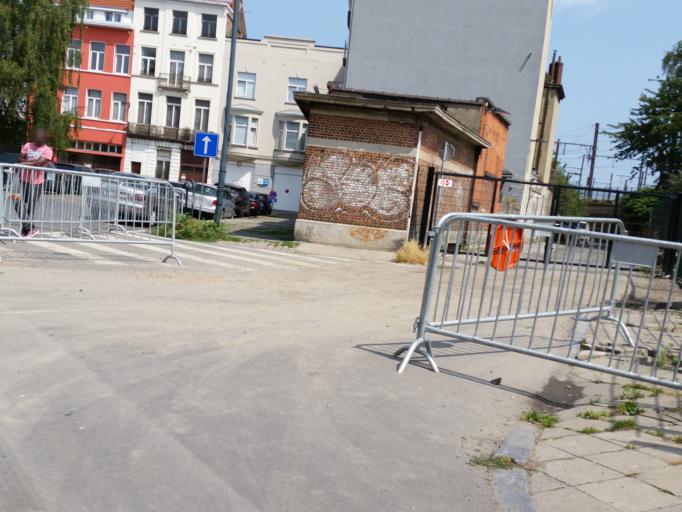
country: BE
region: Brussels Capital
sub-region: Bruxelles-Capitale
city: Brussels
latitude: 50.8704
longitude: 4.3650
